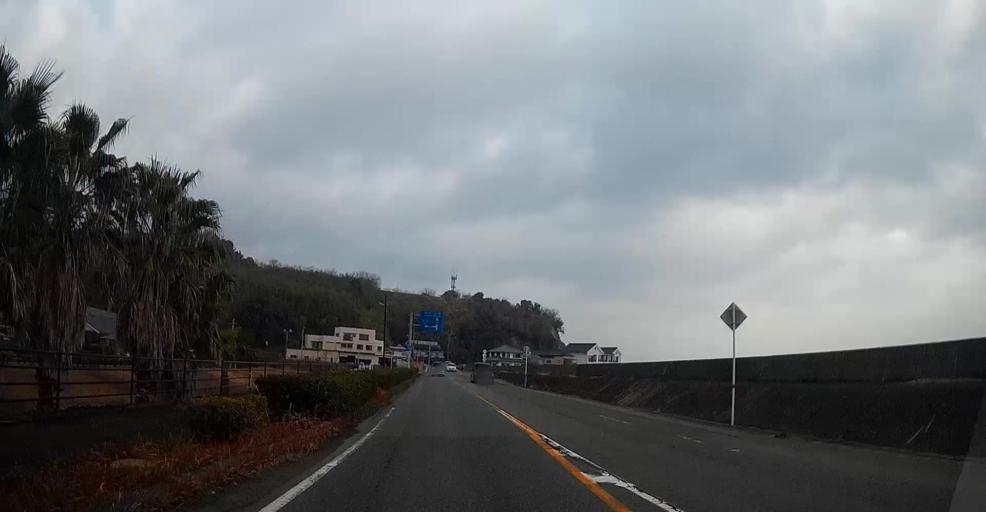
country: JP
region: Kumamoto
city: Matsubase
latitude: 32.6297
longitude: 130.6091
